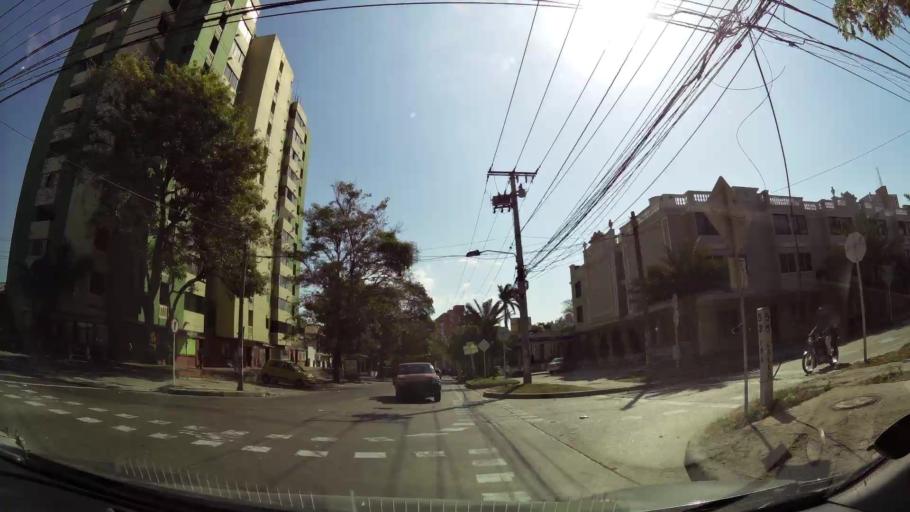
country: CO
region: Atlantico
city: Barranquilla
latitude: 10.9918
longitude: -74.7912
